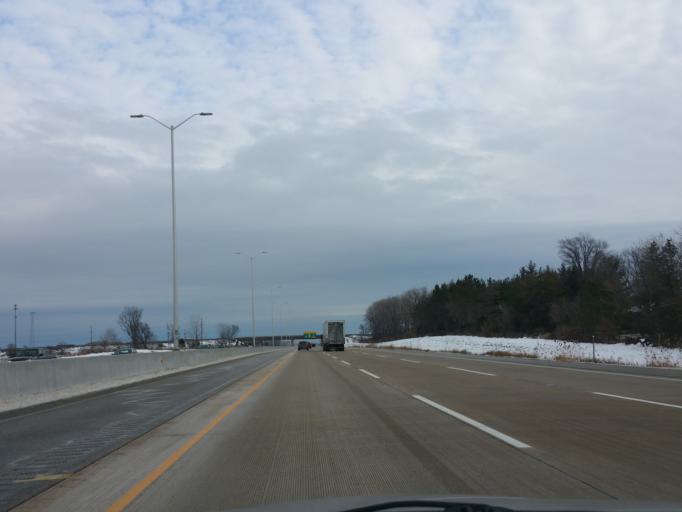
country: US
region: Illinois
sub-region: McHenry County
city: Marengo
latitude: 42.1795
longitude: -88.6233
